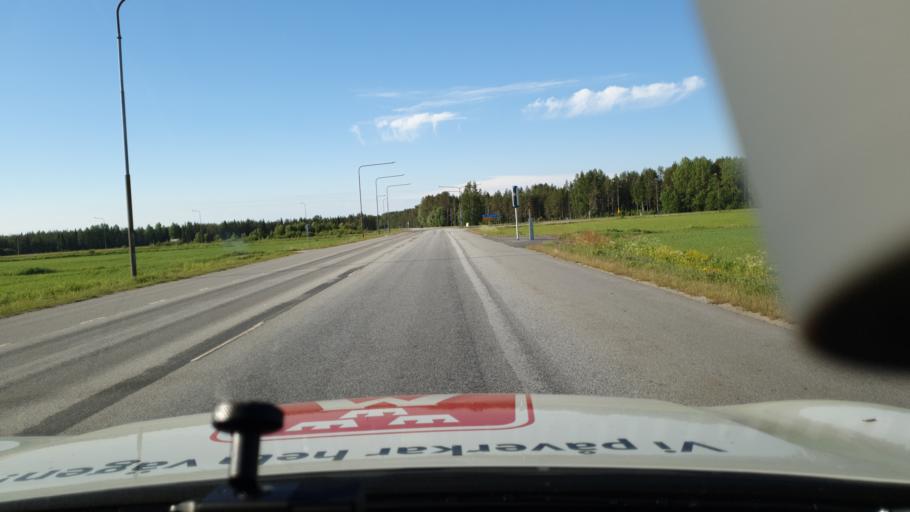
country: SE
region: Vaesterbotten
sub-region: Umea Kommun
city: Roback
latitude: 63.7783
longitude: 20.2029
